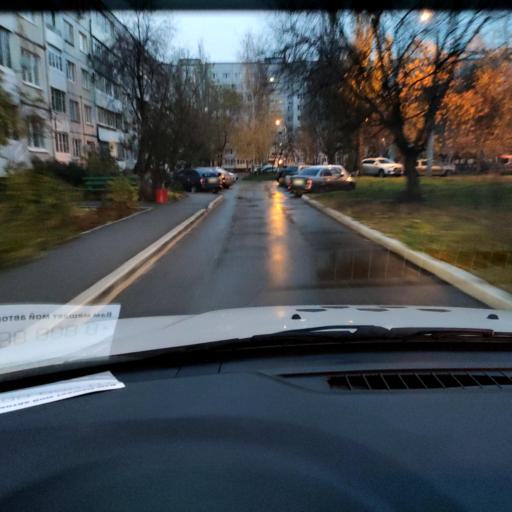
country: RU
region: Samara
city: Tol'yatti
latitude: 53.5083
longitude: 49.4411
